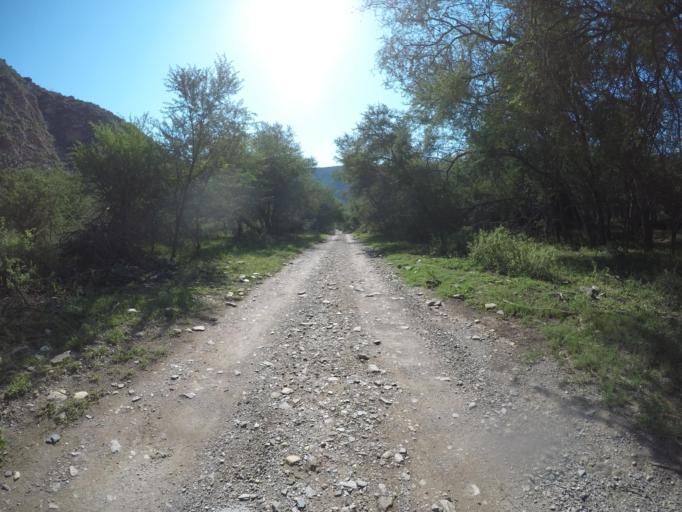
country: ZA
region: Eastern Cape
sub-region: Cacadu District Municipality
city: Kareedouw
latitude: -33.6582
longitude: 24.3662
